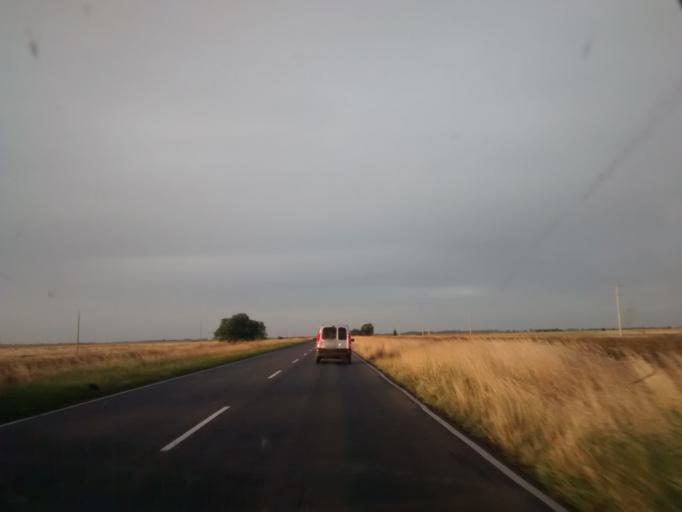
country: AR
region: Buenos Aires
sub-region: Partido de General Belgrano
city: General Belgrano
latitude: -35.9437
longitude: -58.6203
